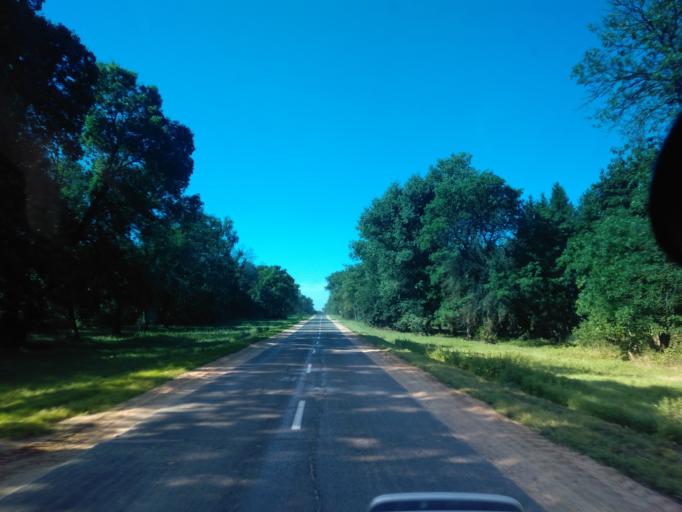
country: BY
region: Minsk
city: Stan'kava
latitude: 53.6361
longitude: 27.2822
